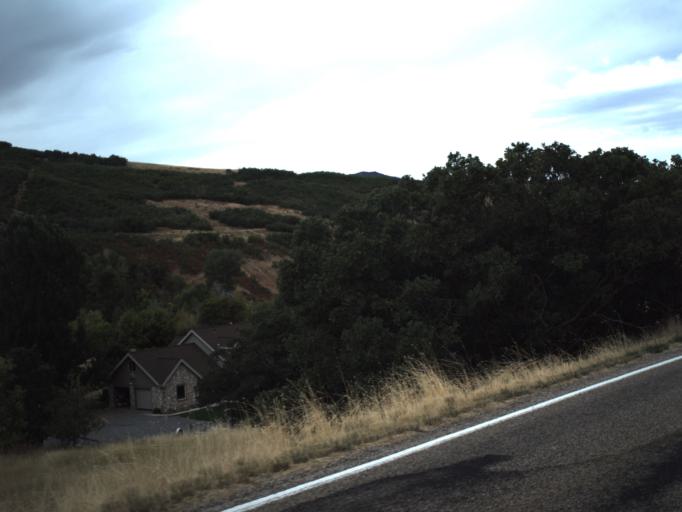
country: US
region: Utah
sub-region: Morgan County
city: Morgan
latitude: 40.9460
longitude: -111.6529
